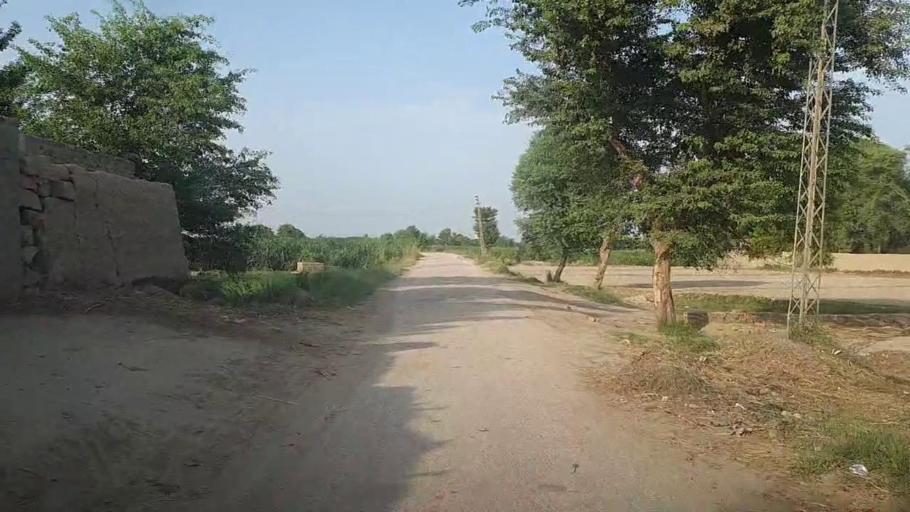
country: PK
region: Sindh
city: Ubauro
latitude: 28.3207
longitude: 69.7943
